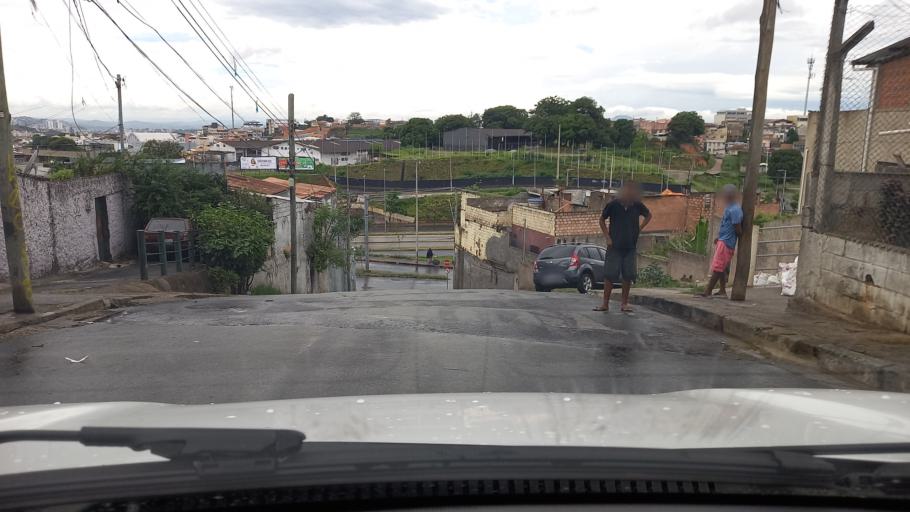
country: BR
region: Minas Gerais
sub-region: Belo Horizonte
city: Belo Horizonte
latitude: -19.8998
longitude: -43.9479
